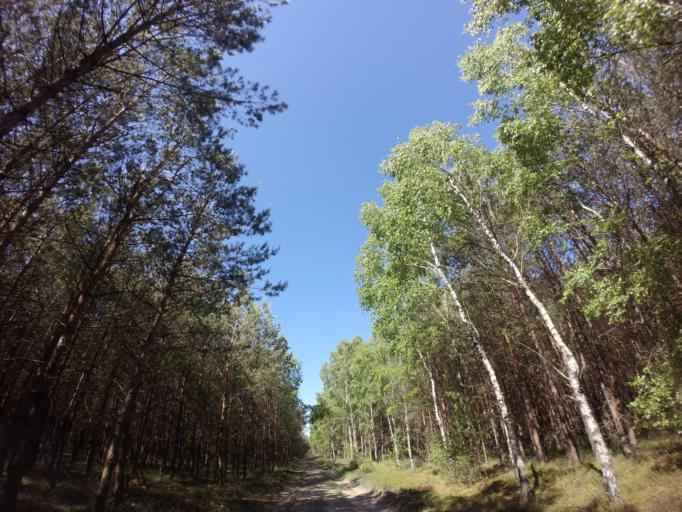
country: PL
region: West Pomeranian Voivodeship
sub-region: Powiat drawski
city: Kalisz Pomorski
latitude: 53.1531
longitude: 15.9405
